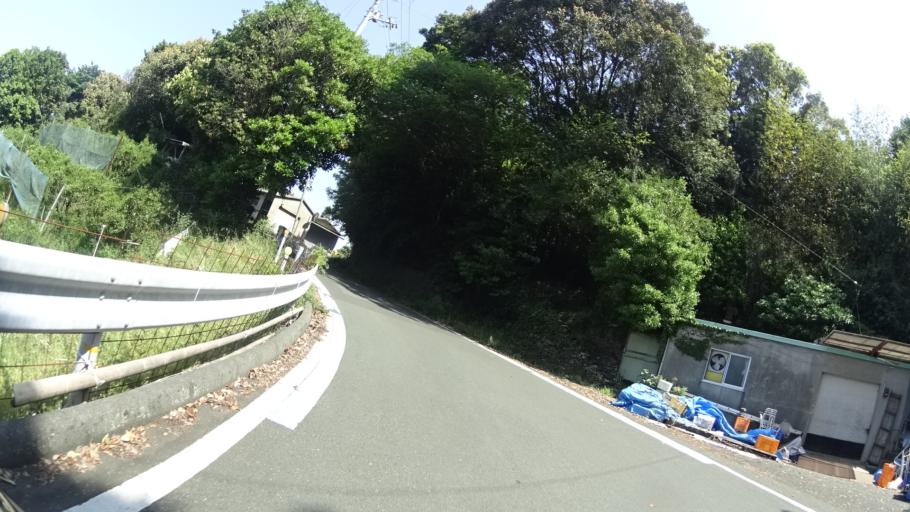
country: JP
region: Ehime
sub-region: Nishiuwa-gun
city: Ikata-cho
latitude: 33.3741
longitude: 132.0560
